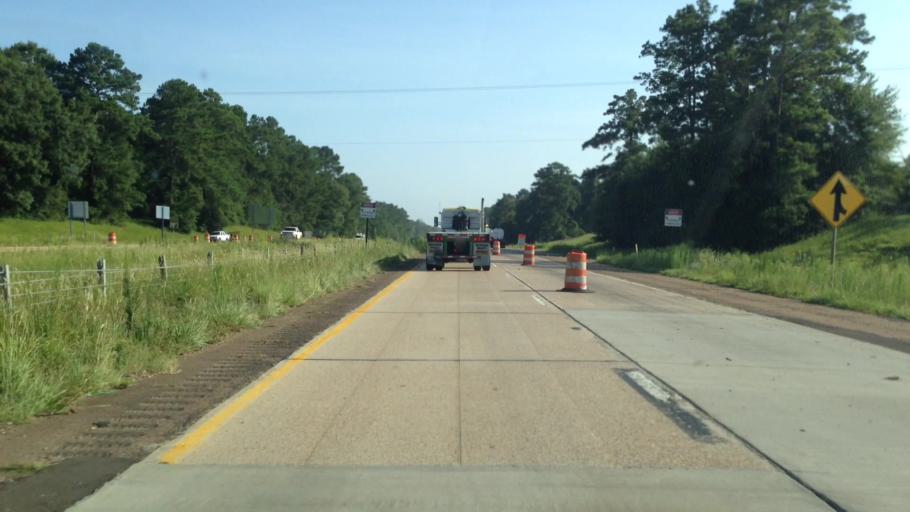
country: US
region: Mississippi
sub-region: Pike County
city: McComb
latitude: 31.2229
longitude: -90.4827
